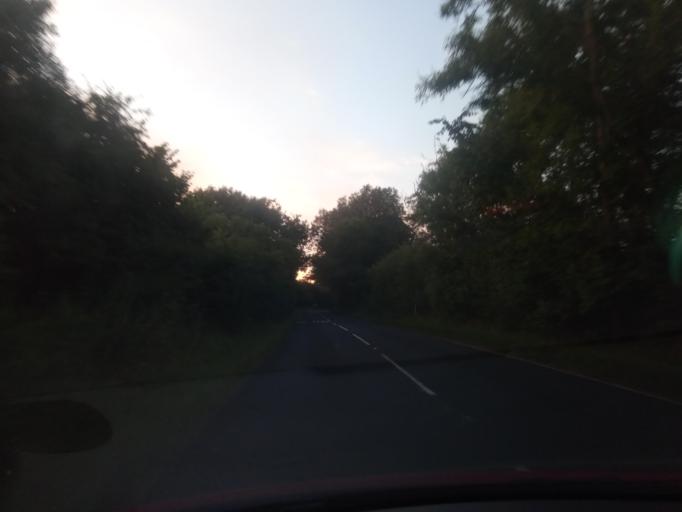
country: GB
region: England
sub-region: Northumberland
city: Bardon Mill
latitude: 54.9416
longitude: -2.2854
